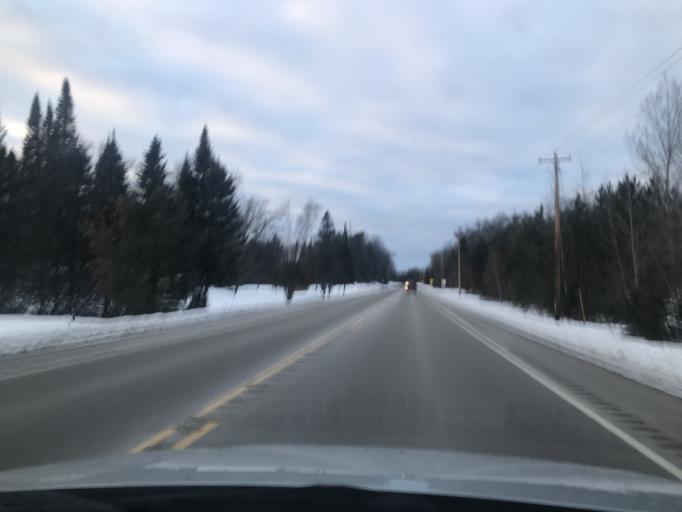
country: US
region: Wisconsin
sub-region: Marinette County
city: Peshtigo
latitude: 45.1632
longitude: -87.7254
